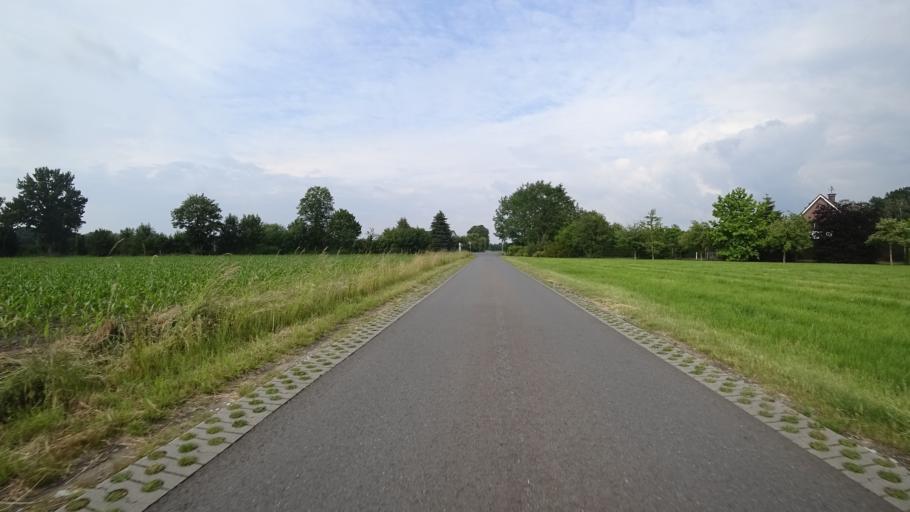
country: DE
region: North Rhine-Westphalia
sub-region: Regierungsbezirk Detmold
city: Guetersloh
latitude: 51.9503
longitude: 8.3517
